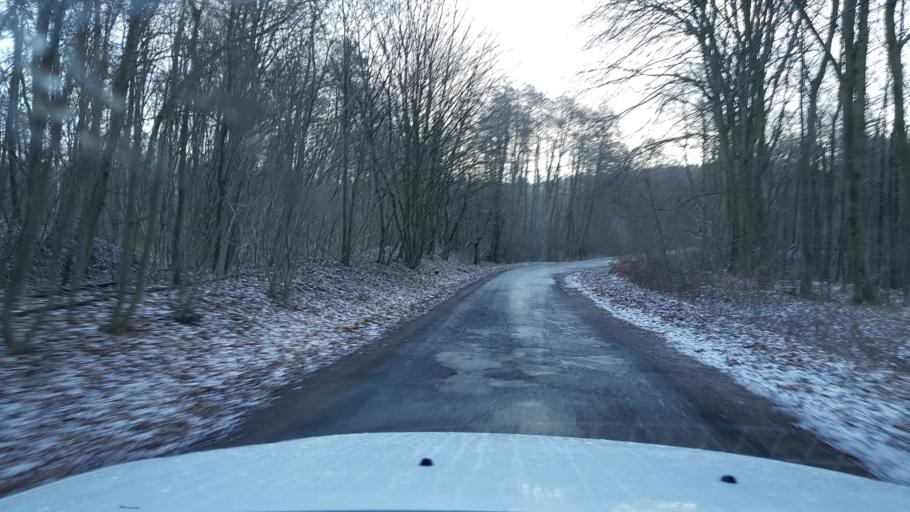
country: PL
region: West Pomeranian Voivodeship
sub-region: Powiat gryficki
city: Trzebiatow
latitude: 54.0480
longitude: 15.3180
